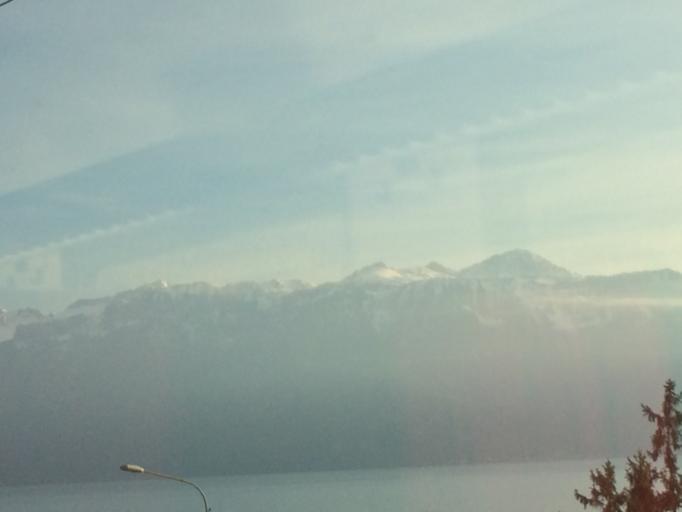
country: CH
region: Vaud
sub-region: Lavaux-Oron District
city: Lutry
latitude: 46.4976
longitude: 6.7030
